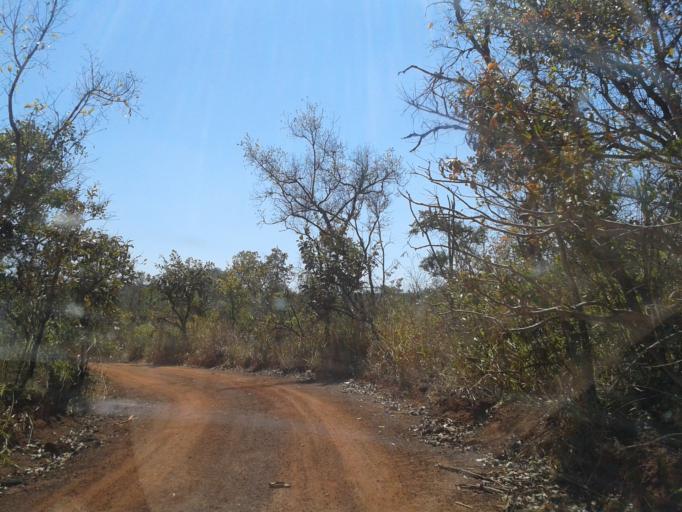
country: BR
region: Minas Gerais
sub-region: Monte Alegre De Minas
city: Monte Alegre de Minas
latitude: -18.8267
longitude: -49.1113
